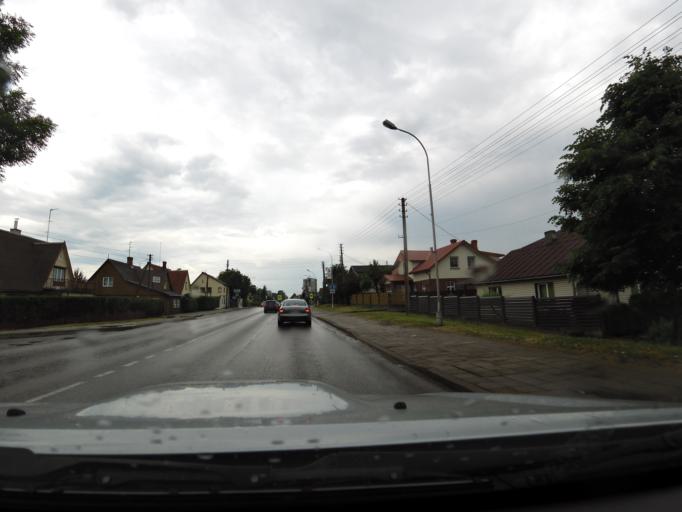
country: LT
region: Marijampoles apskritis
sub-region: Marijampole Municipality
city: Marijampole
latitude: 54.5598
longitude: 23.3434
